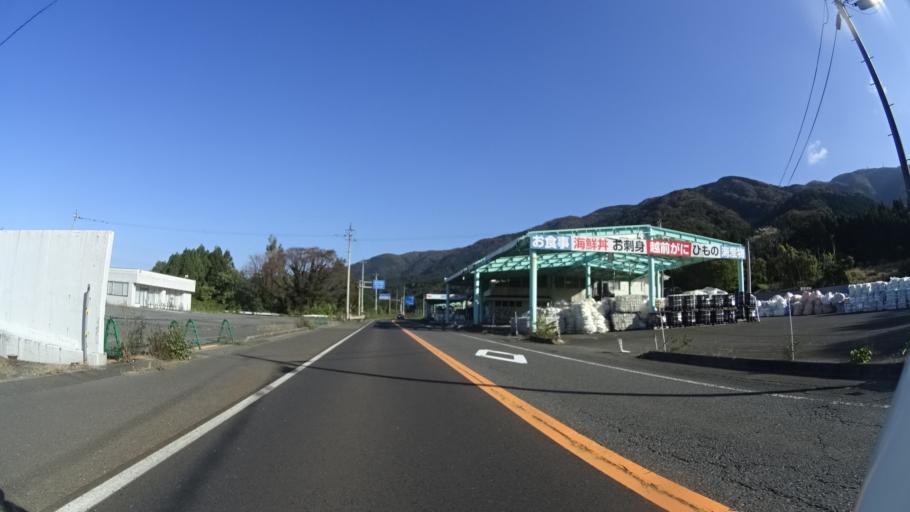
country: JP
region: Fukui
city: Tsuruga
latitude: 35.7409
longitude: 136.1016
